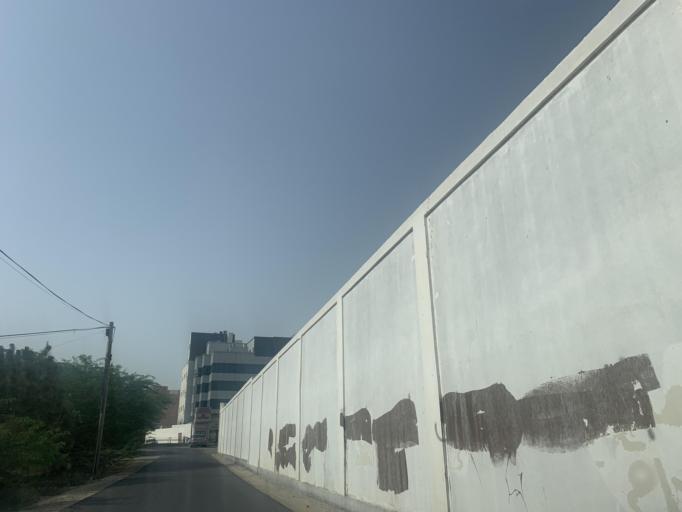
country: BH
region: Manama
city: Jidd Hafs
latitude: 26.2149
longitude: 50.4706
